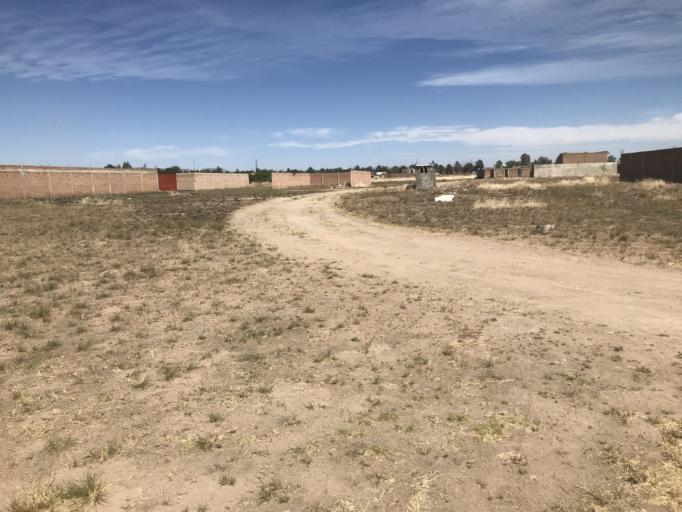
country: MX
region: Durango
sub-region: Durango
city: Sebastian Lerdo de Tejada
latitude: 23.9764
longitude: -104.6562
